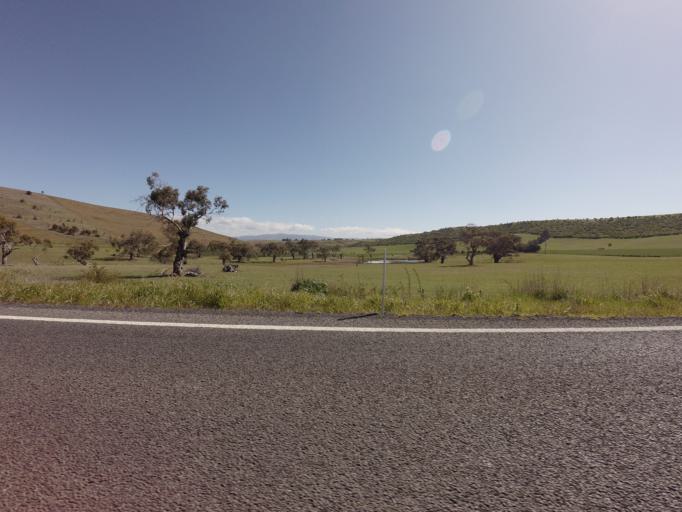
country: AU
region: Tasmania
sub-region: Derwent Valley
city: New Norfolk
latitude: -42.5703
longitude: 146.8810
